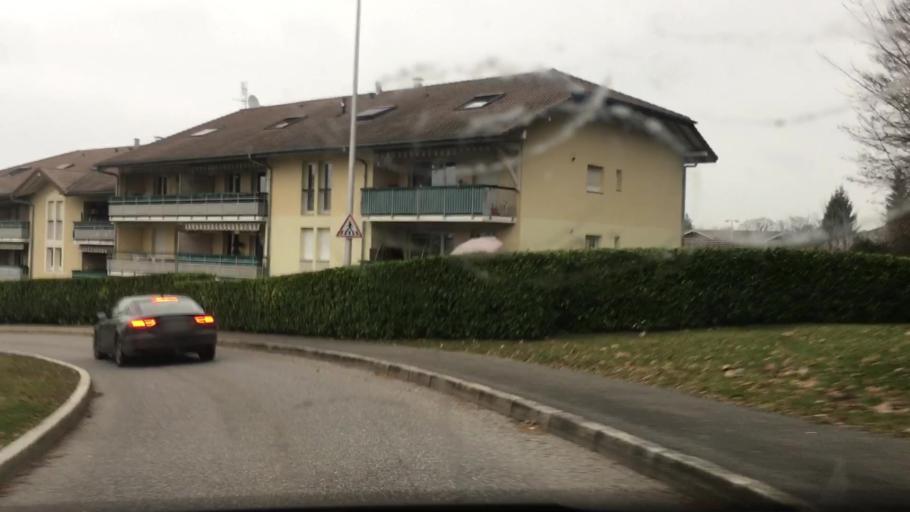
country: FR
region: Rhone-Alpes
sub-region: Departement de la Haute-Savoie
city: Publier
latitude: 46.3891
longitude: 6.5466
